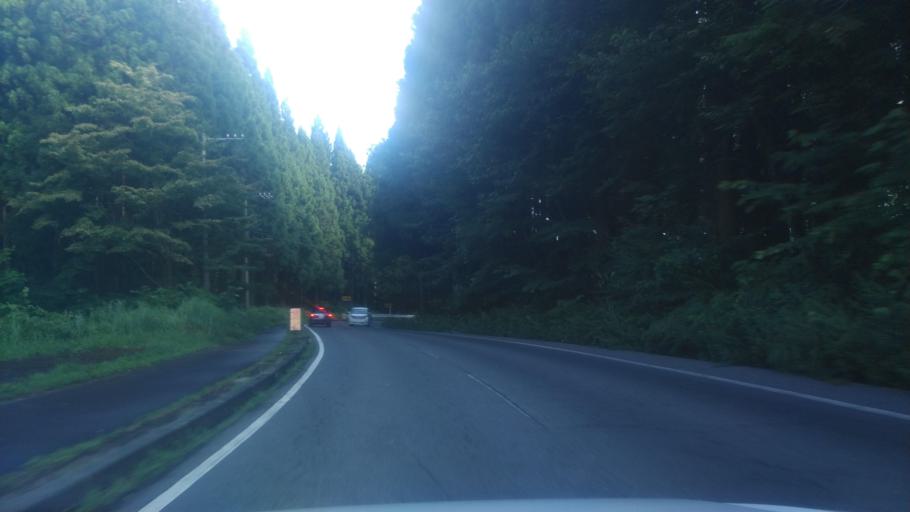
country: JP
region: Nagano
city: Nagano-shi
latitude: 36.7274
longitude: 138.2101
